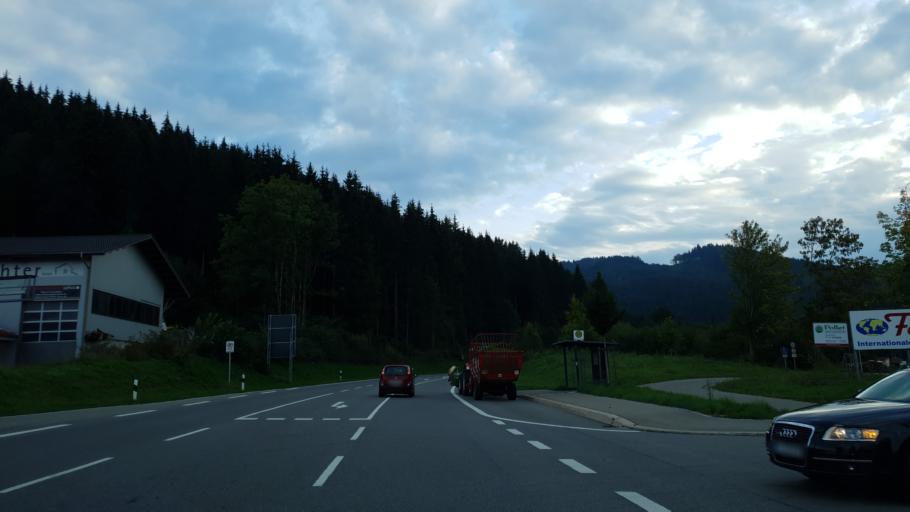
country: DE
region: Bavaria
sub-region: Swabia
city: Maierhofen
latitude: 47.6561
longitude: 10.0890
